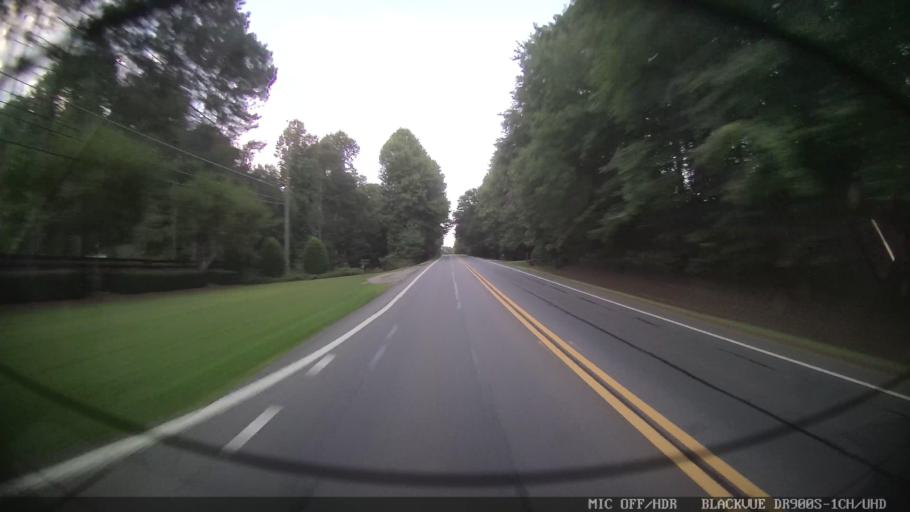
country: US
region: Georgia
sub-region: Cherokee County
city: Ball Ground
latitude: 34.2990
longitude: -84.2485
